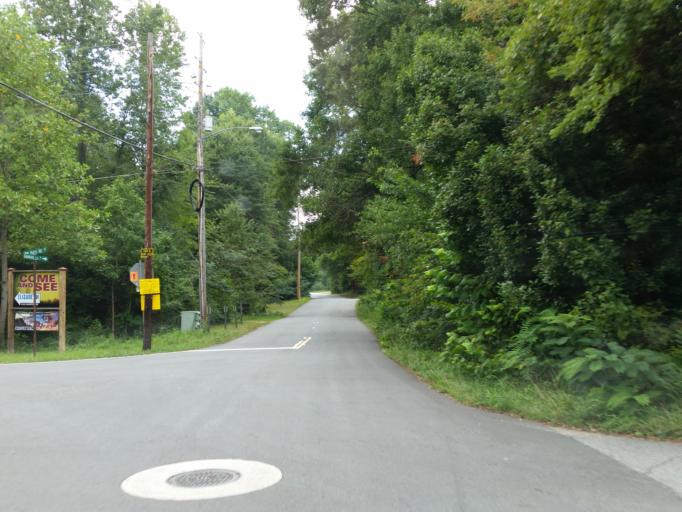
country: US
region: Georgia
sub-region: Cobb County
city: Marietta
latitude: 34.0045
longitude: -84.5353
